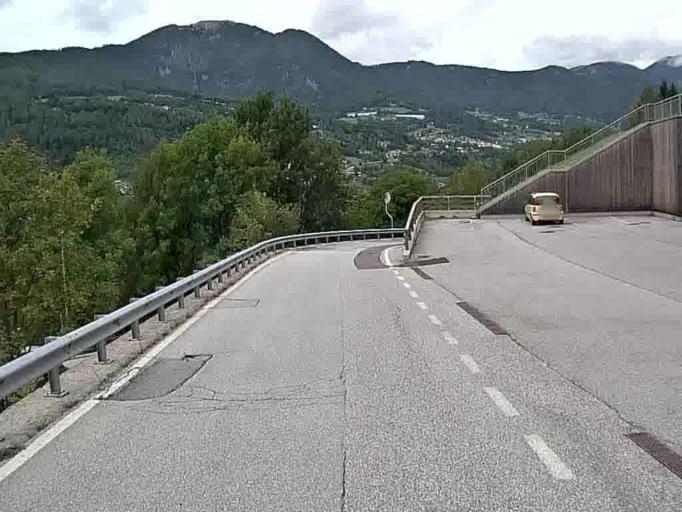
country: IT
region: Trentino-Alto Adige
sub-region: Provincia di Trento
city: Frassilongo
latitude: 46.0856
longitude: 11.2929
